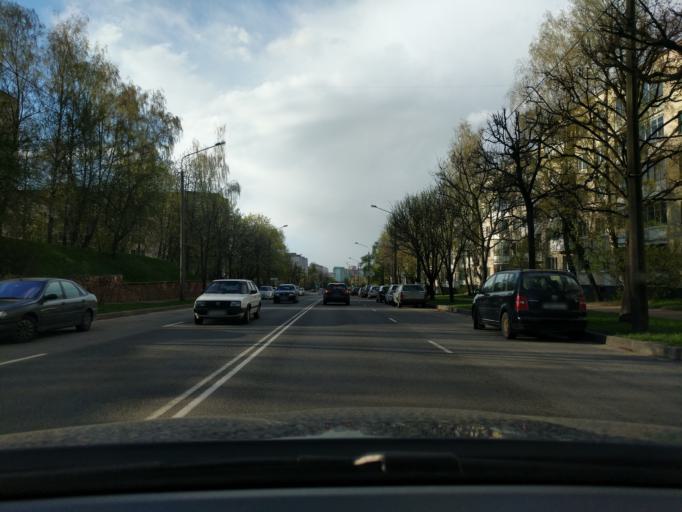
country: BY
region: Minsk
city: Novoye Medvezhino
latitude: 53.9132
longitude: 27.4801
